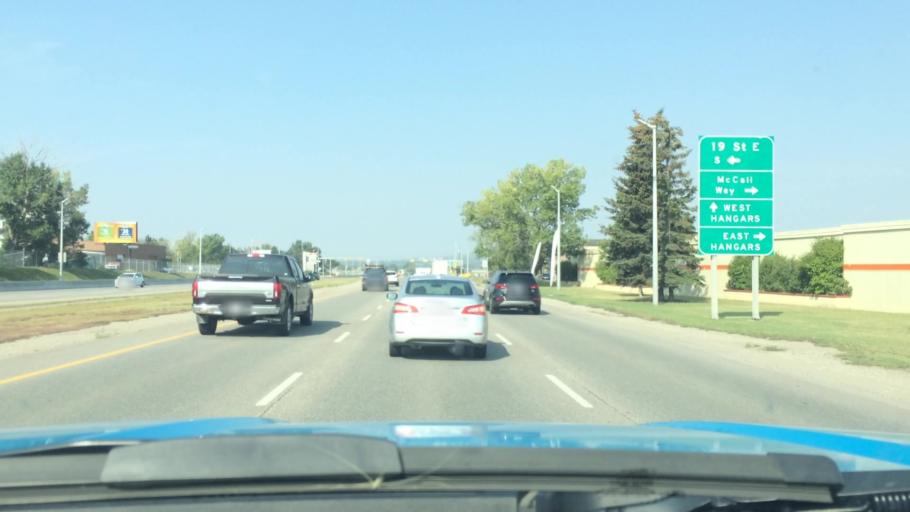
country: CA
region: Alberta
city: Calgary
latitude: 51.0931
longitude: -114.0076
